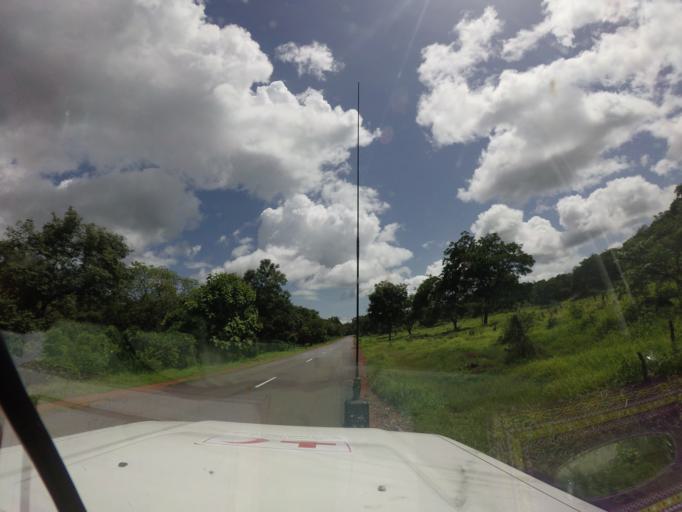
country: SL
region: Northern Province
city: Bindi
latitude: 10.1559
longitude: -11.6777
